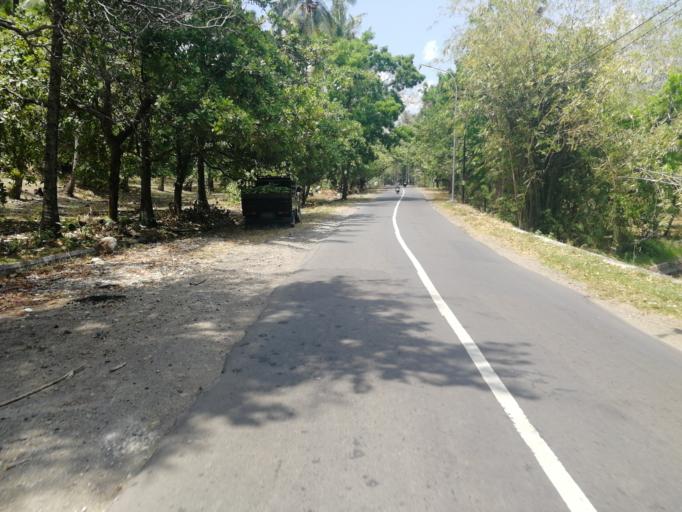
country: ID
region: West Nusa Tenggara
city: Karangsubagan
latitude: -8.4203
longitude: 116.0949
